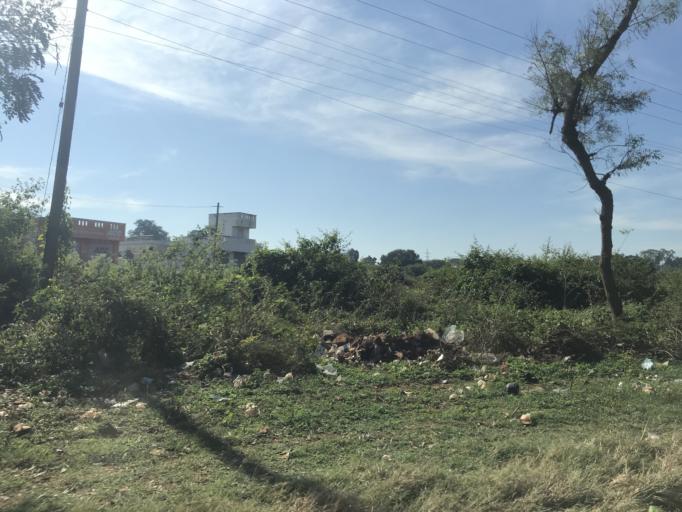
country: IN
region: Karnataka
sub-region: Mysore
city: Mysore
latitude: 12.2234
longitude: 76.5765
